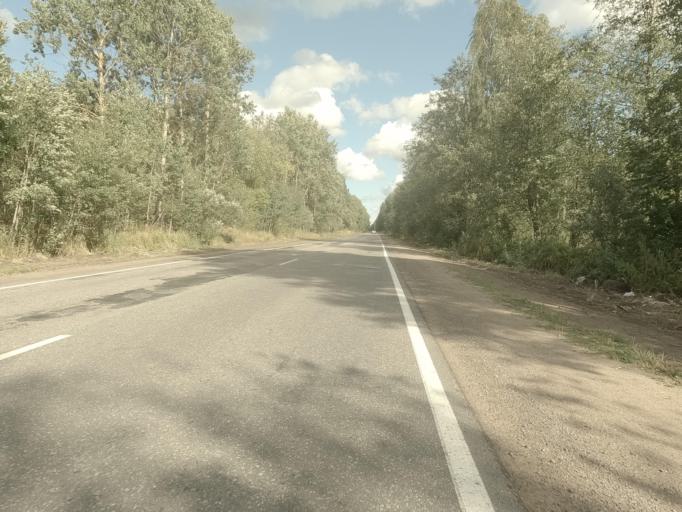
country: RU
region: Leningrad
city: Romanovka
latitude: 60.0231
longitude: 30.7110
